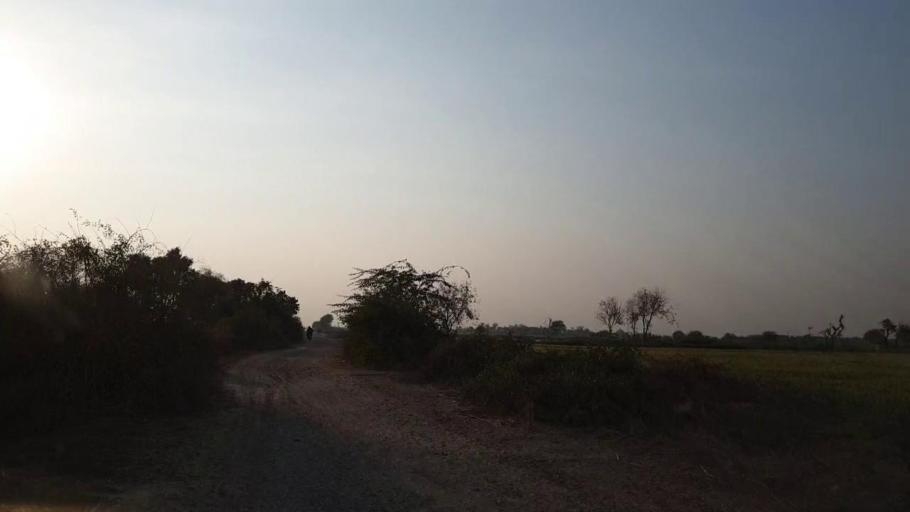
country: PK
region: Sindh
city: Pithoro
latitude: 25.6541
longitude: 69.2261
